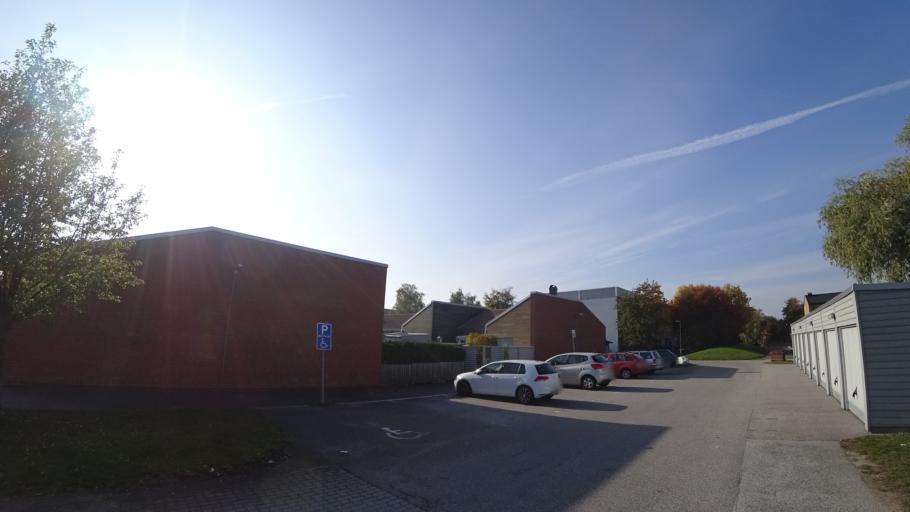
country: SE
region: Skane
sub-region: Staffanstorps Kommun
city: Staffanstorp
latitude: 55.6470
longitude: 13.2011
